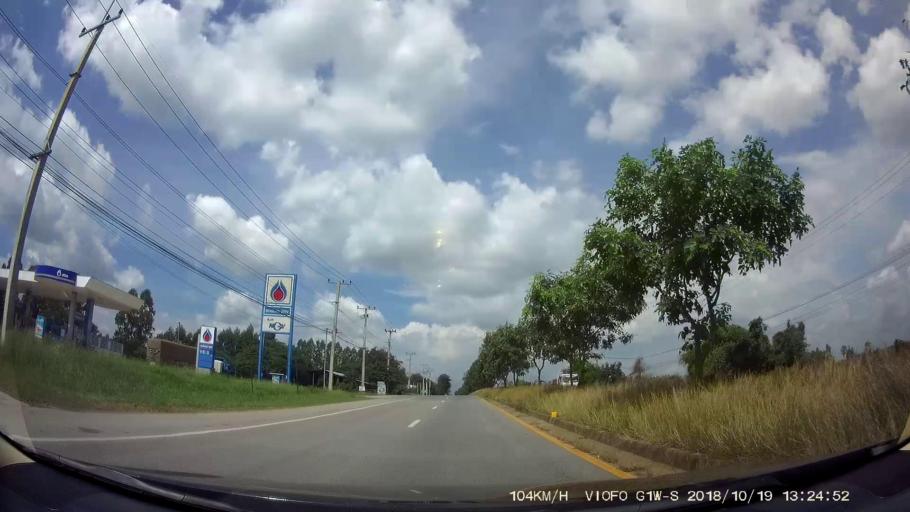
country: TH
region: Chaiyaphum
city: Chatturat
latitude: 15.5133
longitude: 101.8237
